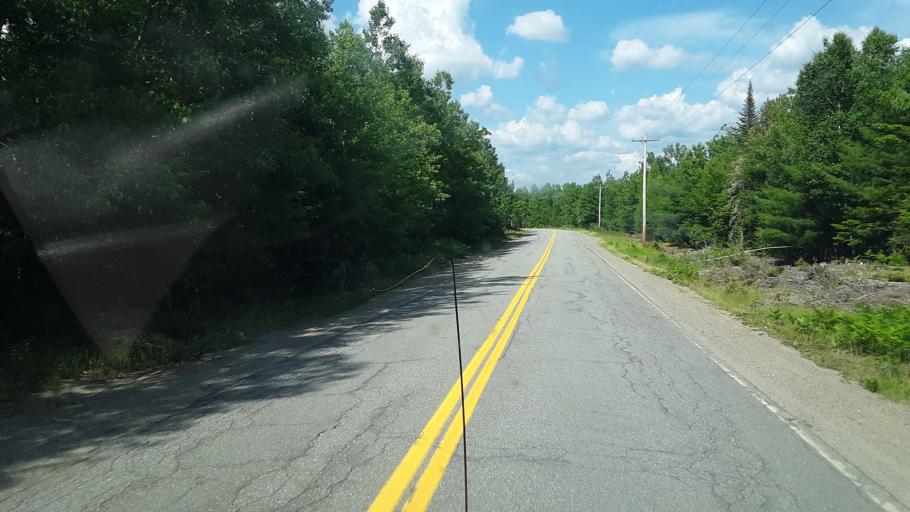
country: US
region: Maine
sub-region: Washington County
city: Calais
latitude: 45.1137
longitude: -67.5061
